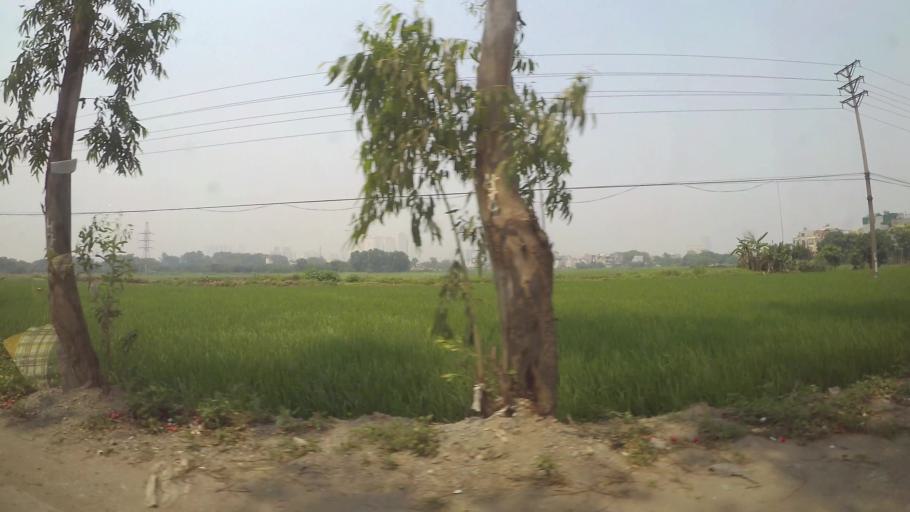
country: VN
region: Ha Noi
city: Van Dien
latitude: 20.9495
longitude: 105.8223
